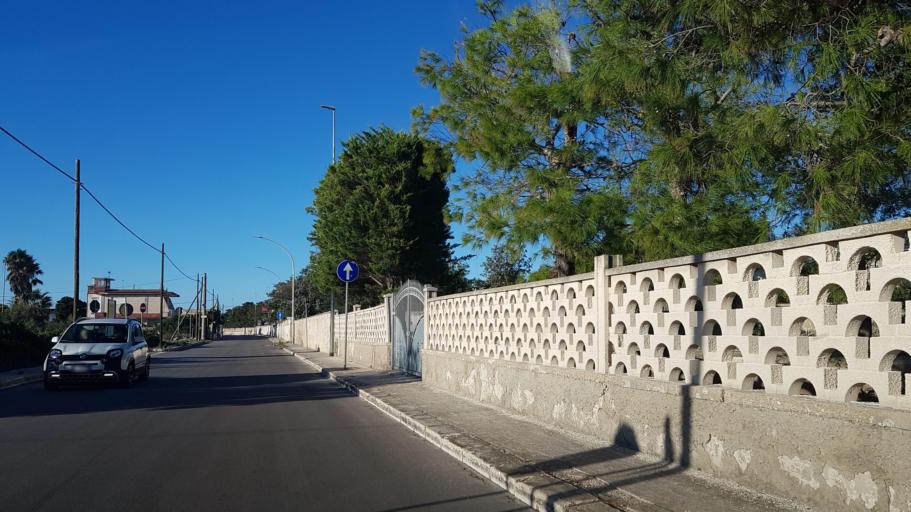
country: IT
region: Apulia
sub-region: Provincia di Lecce
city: Giorgilorio
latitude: 40.4642
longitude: 18.1952
